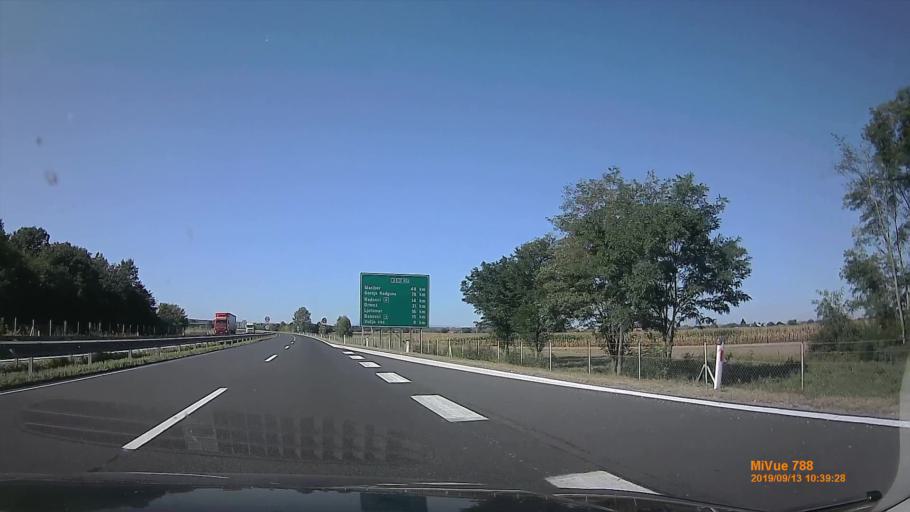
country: SI
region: Murska Sobota
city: Krog
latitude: 46.6326
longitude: 16.1505
